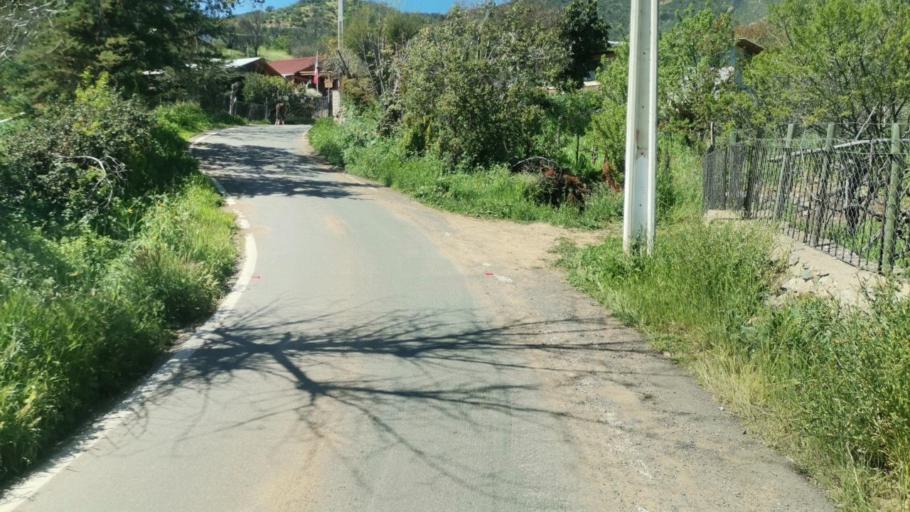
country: CL
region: Santiago Metropolitan
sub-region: Provincia de Chacabuco
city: Lampa
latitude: -33.1948
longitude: -71.0943
